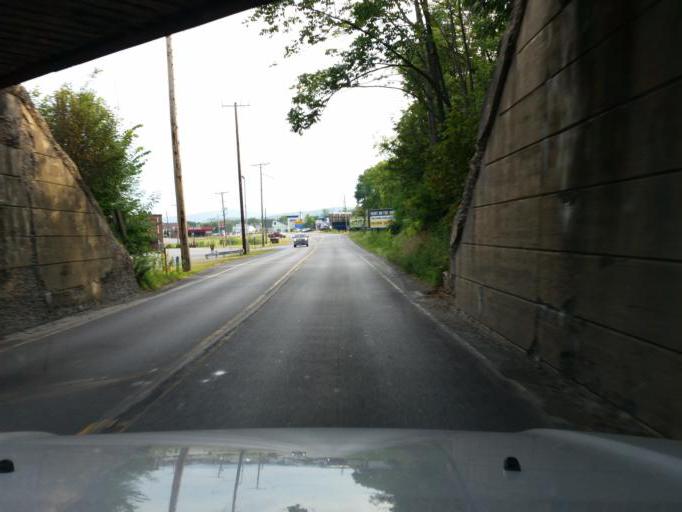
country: US
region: Pennsylvania
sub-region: Blair County
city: Duncansville
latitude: 40.4565
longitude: -78.4282
